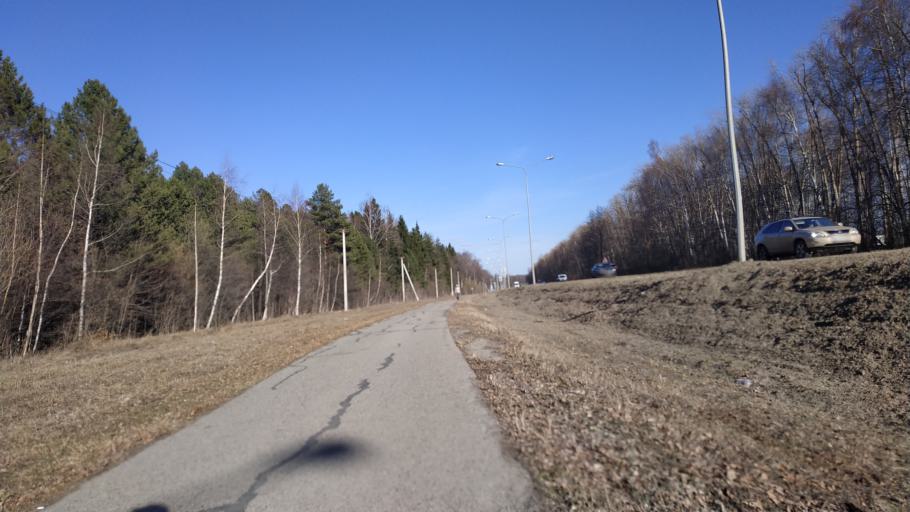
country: RU
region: Chuvashia
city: Ishley
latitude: 56.1349
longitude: 47.0963
